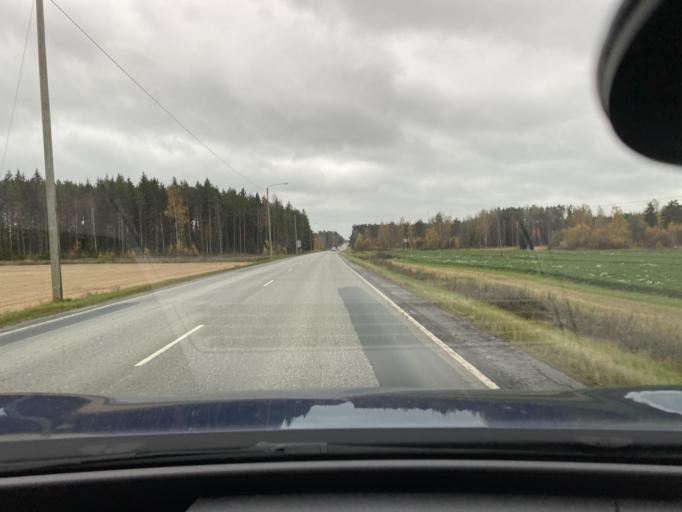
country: FI
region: Varsinais-Suomi
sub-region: Vakka-Suomi
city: Laitila
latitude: 60.9743
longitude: 21.5931
